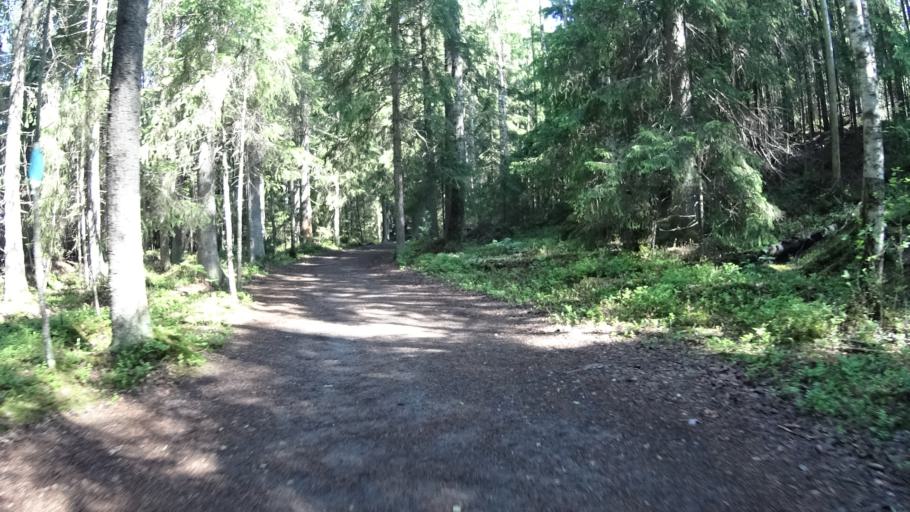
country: FI
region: Uusimaa
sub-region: Helsinki
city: Kauniainen
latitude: 60.3288
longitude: 24.6869
